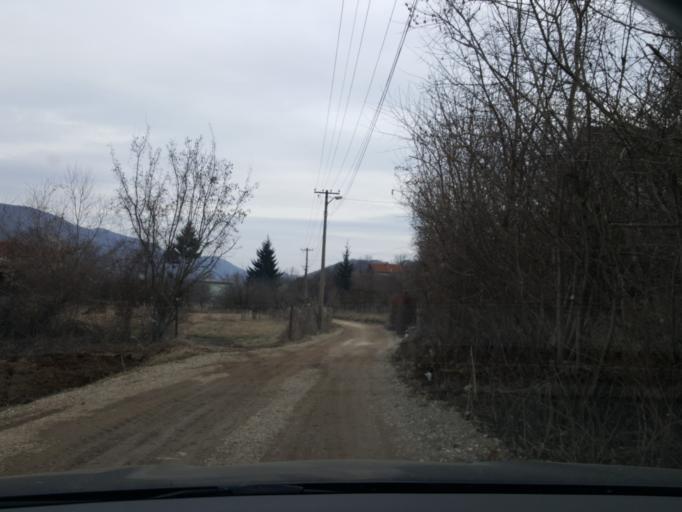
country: RS
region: Central Serbia
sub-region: Pirotski Okrug
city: Dimitrovgrad
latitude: 43.0071
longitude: 22.7550
